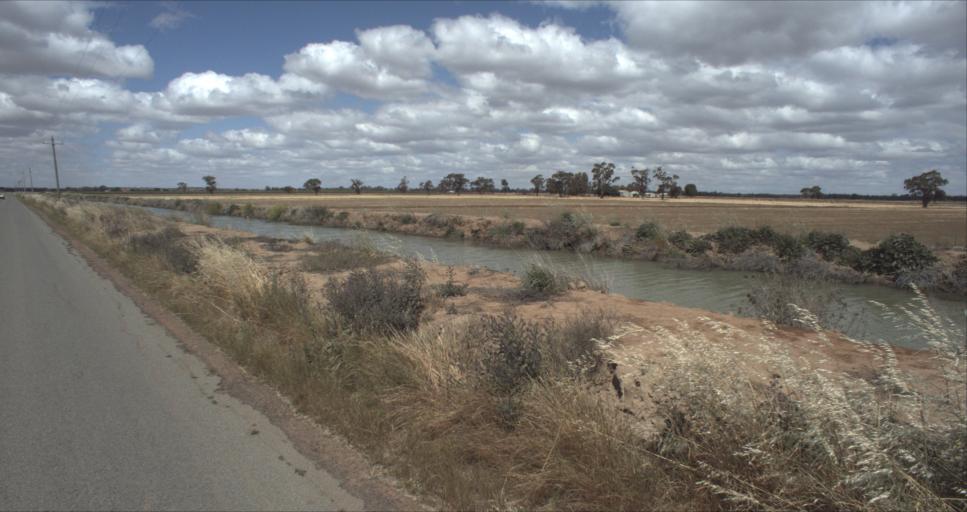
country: AU
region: New South Wales
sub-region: Leeton
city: Leeton
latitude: -34.5872
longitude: 146.3731
